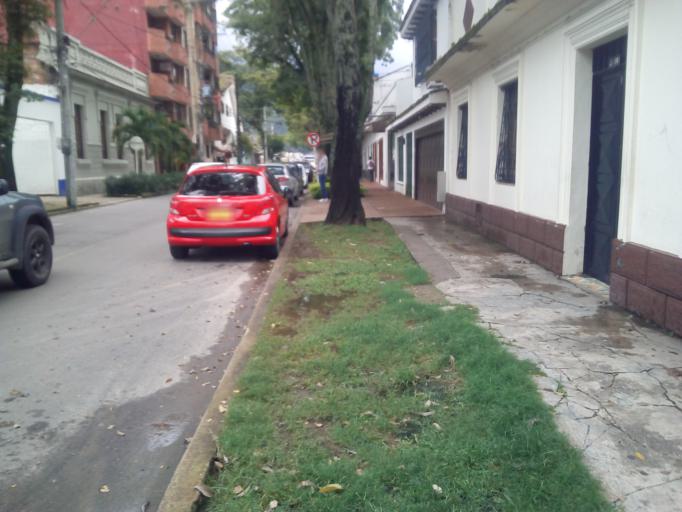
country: CO
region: Tolima
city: Ibague
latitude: 4.4458
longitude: -75.2452
